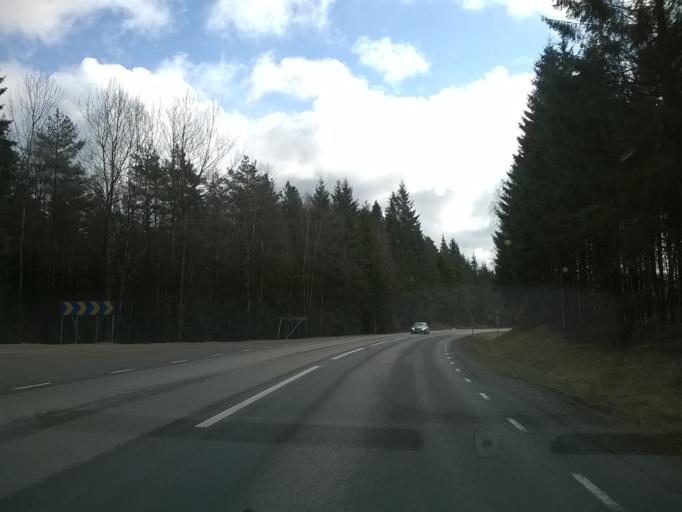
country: SE
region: Vaestra Goetaland
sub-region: Marks Kommun
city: Horred
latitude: 57.1572
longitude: 12.6676
